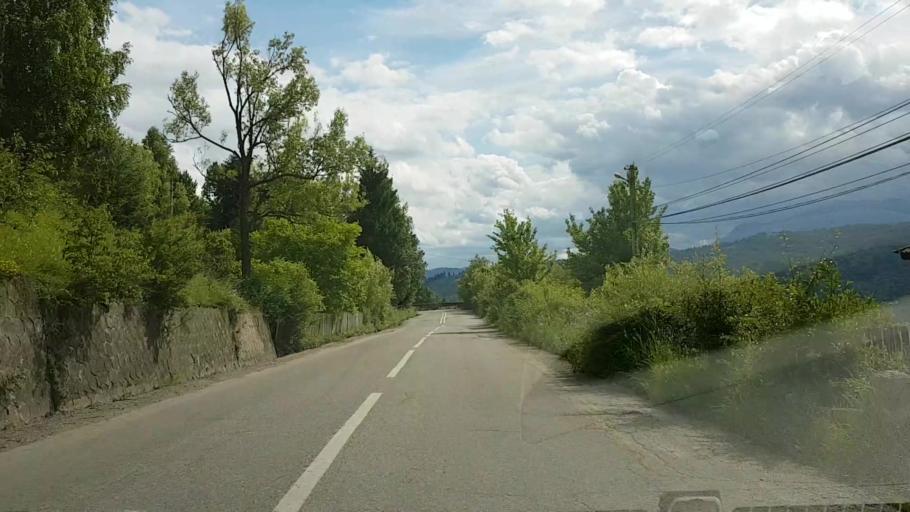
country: RO
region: Neamt
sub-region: Comuna Hangu
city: Hangu
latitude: 47.0316
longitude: 26.0664
